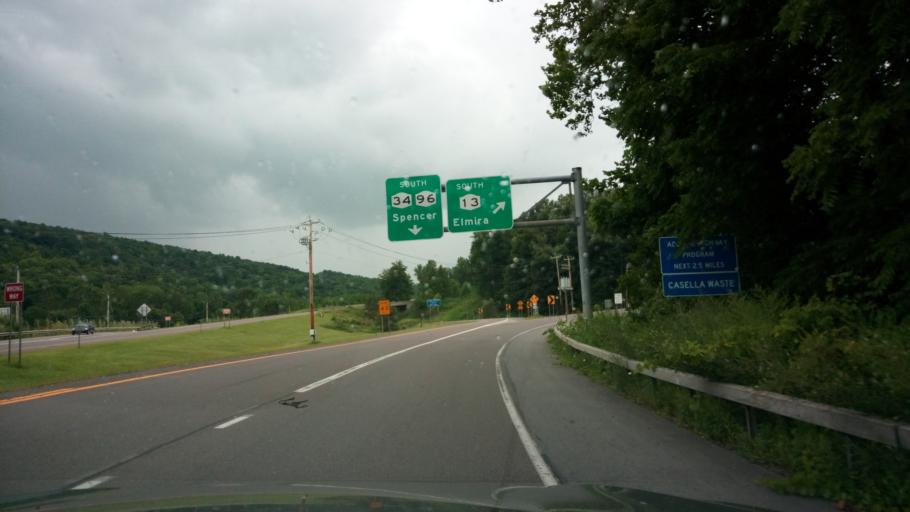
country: US
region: New York
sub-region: Tompkins County
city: South Hill
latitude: 42.3979
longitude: -76.5462
